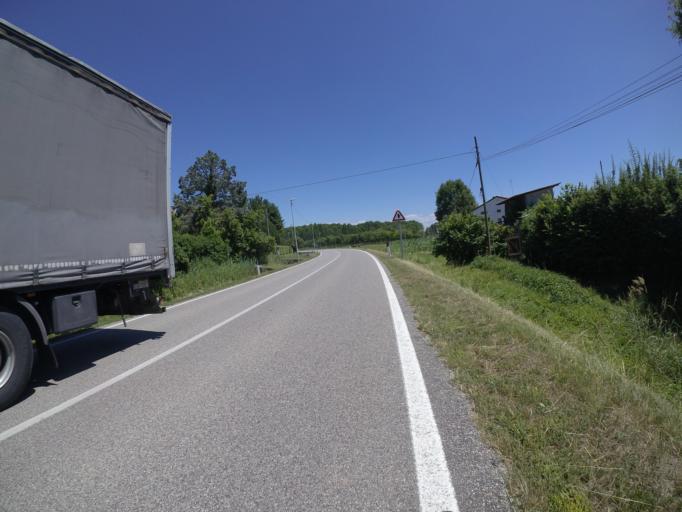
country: IT
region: Friuli Venezia Giulia
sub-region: Provincia di Udine
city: Rivignano
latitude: 45.8849
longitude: 13.0731
